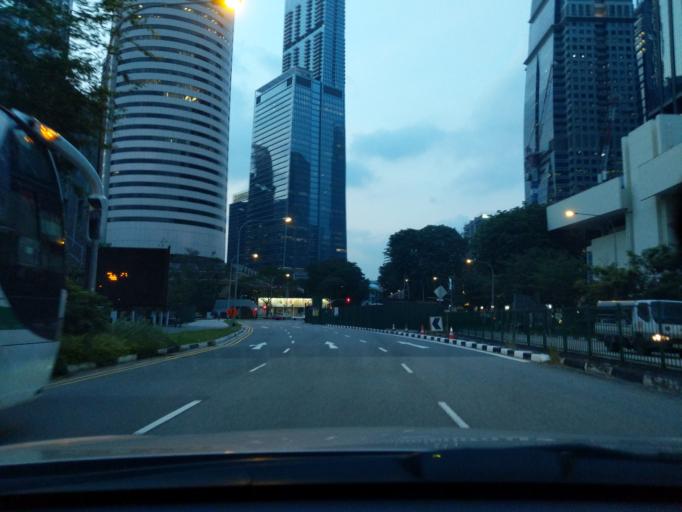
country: SG
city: Singapore
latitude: 1.2753
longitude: 103.8492
